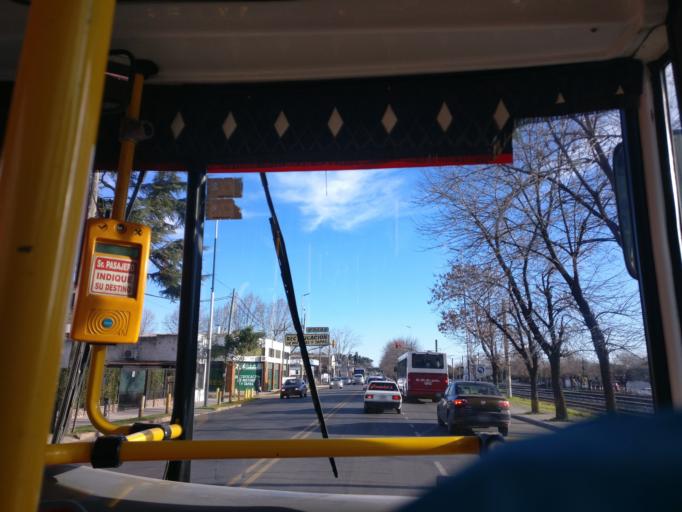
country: AR
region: Buenos Aires
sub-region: Partido de Ezeiza
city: Ezeiza
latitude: -34.8579
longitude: -58.5273
